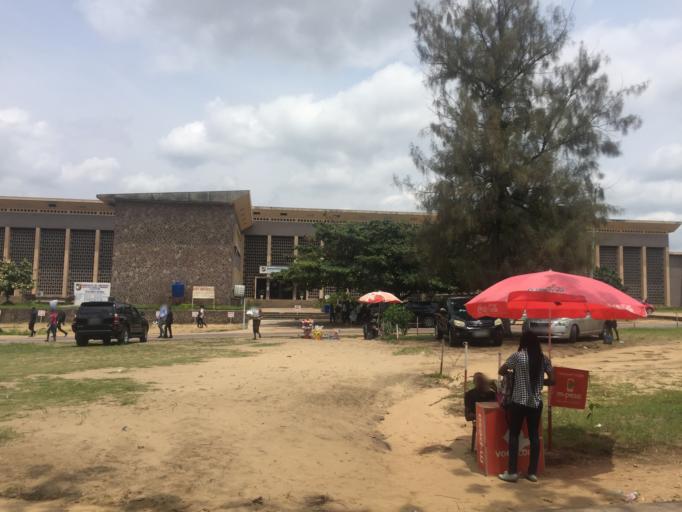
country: CD
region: Kinshasa
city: Masina
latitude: -4.4207
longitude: 15.3090
